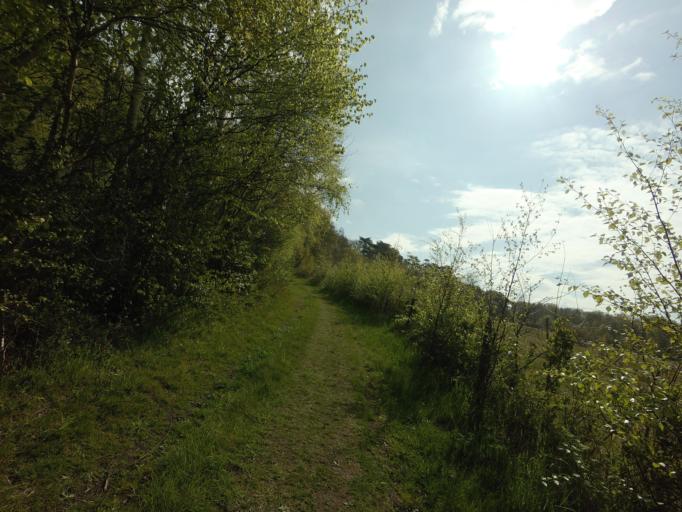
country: DK
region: Capital Region
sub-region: Helsingor Kommune
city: Hellebaek
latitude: 56.1189
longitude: 12.6138
